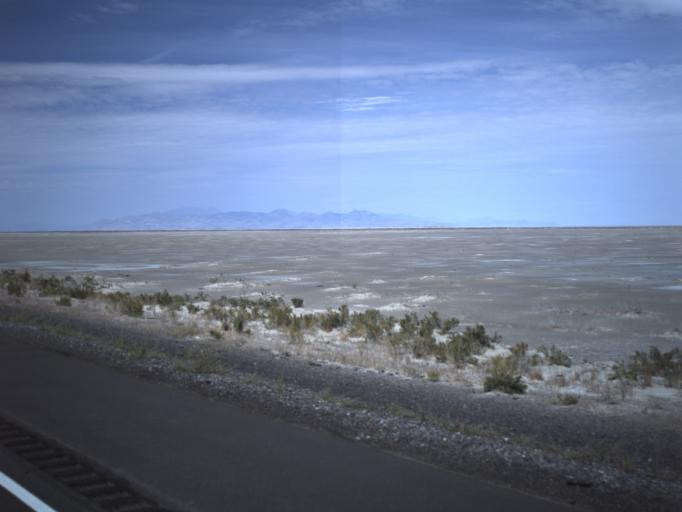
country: US
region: Utah
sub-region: Tooele County
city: Wendover
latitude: 40.7287
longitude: -113.3536
